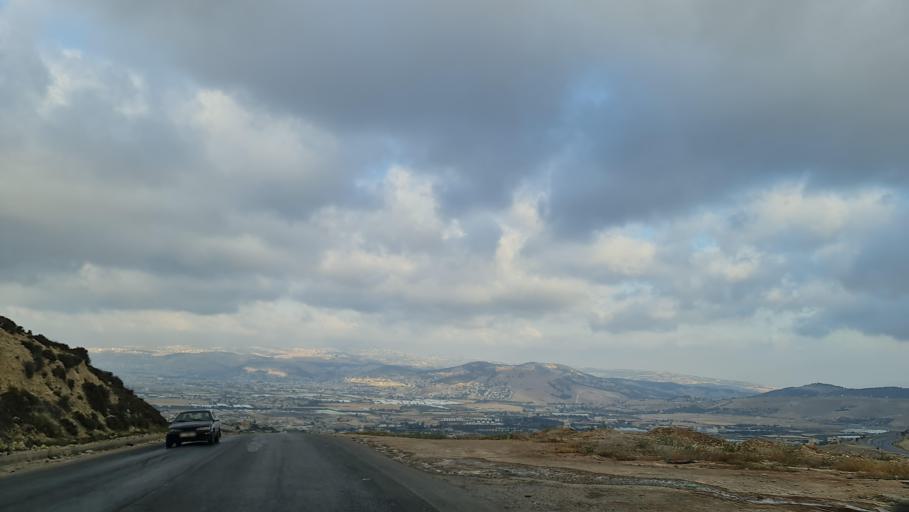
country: JO
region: Amman
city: Al Jubayhah
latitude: 32.0945
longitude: 35.9014
